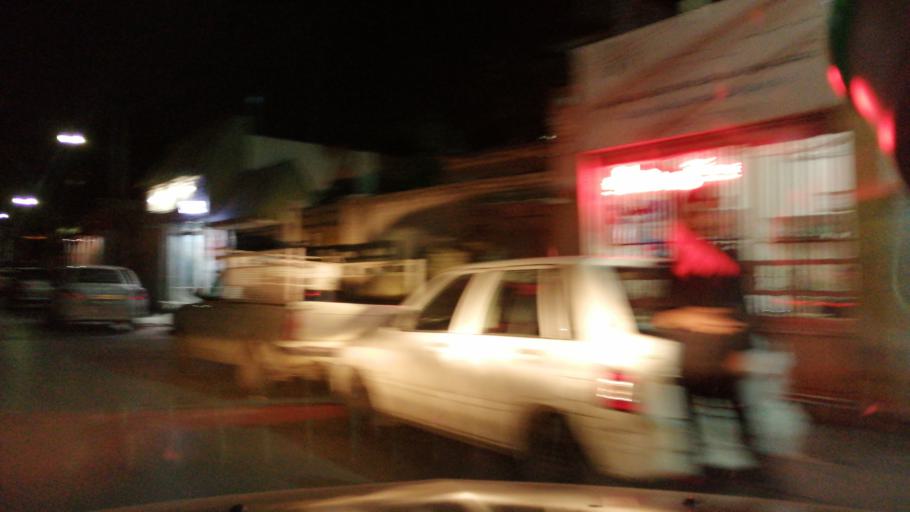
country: IR
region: Razavi Khorasan
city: Mashhad
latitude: 36.3075
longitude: 59.6049
